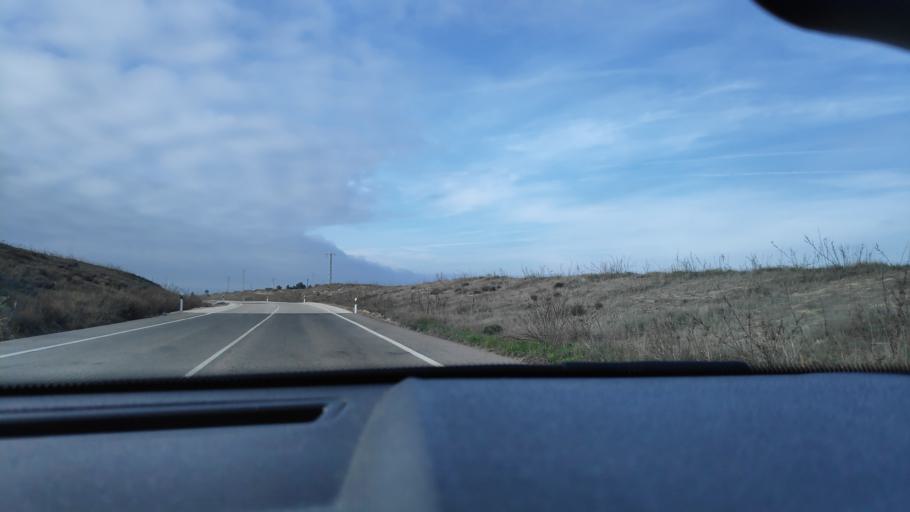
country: ES
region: Andalusia
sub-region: Provincia de Jaen
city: Linares
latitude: 38.0826
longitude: -3.6304
